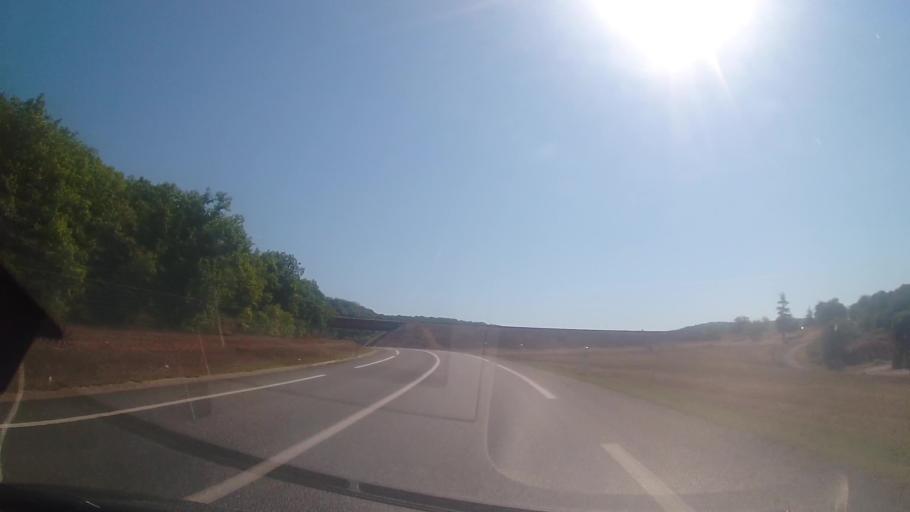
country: FR
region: Midi-Pyrenees
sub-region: Departement du Lot
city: Souillac
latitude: 44.9044
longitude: 1.4976
